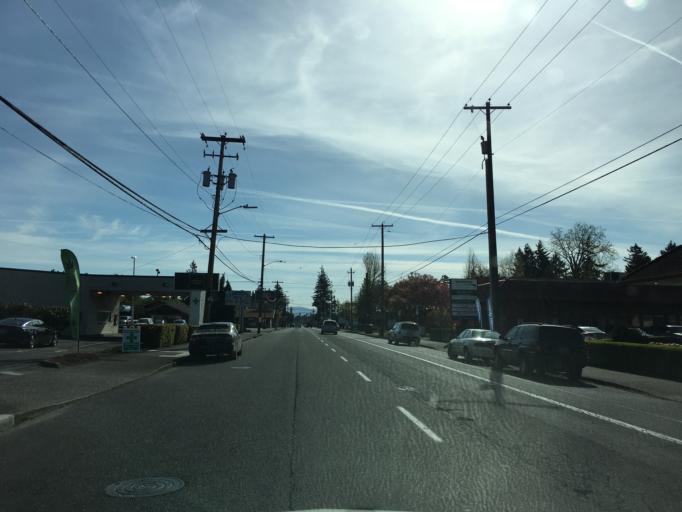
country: US
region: Oregon
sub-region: Multnomah County
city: Lents
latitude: 45.5335
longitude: -122.5527
